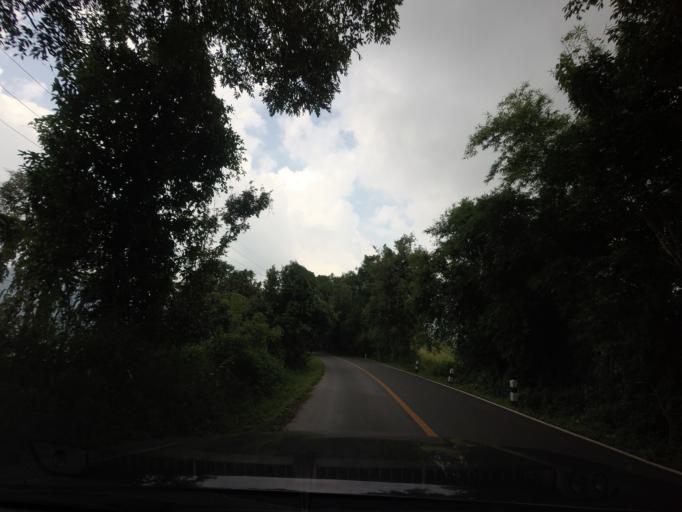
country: TH
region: Nan
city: Bo Kluea
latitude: 19.1905
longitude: 101.0447
